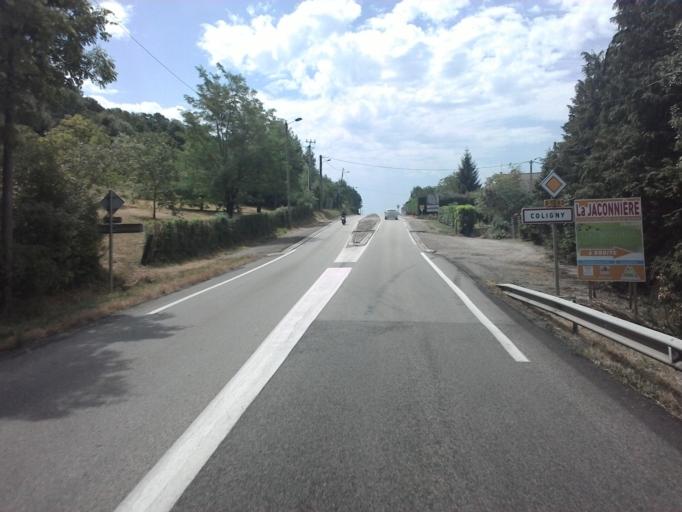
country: FR
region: Rhone-Alpes
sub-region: Departement de l'Ain
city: Coligny
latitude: 46.3939
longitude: 5.3479
